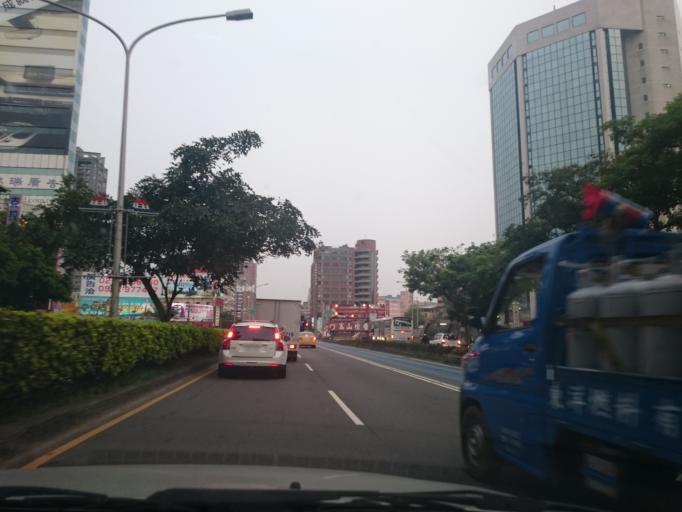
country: TW
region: Taiwan
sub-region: Taichung City
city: Taichung
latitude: 24.1515
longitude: 120.6685
